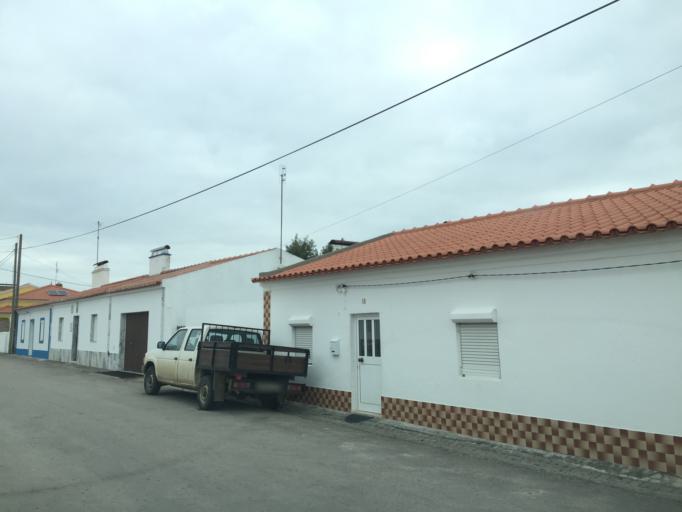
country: PT
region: Portalegre
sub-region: Fronteira
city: Vale da Amoreira
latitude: 39.0451
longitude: -7.7635
